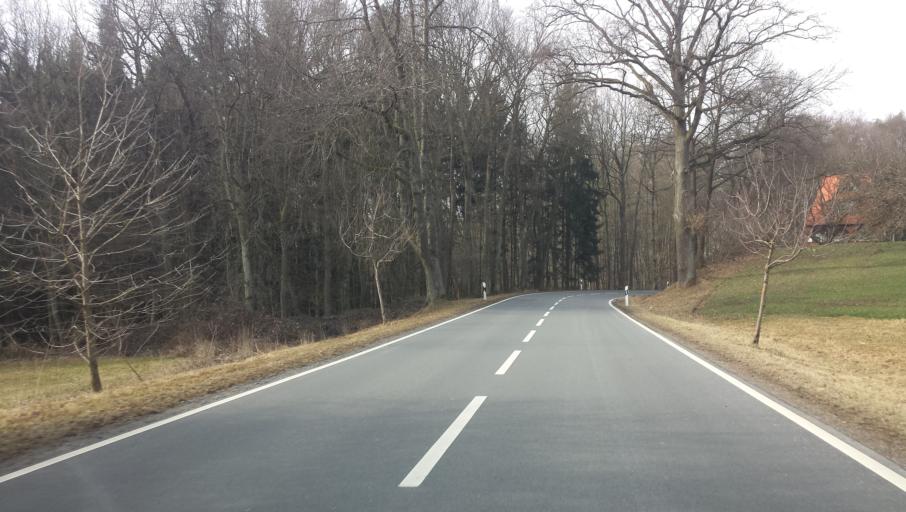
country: DE
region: Hesse
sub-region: Regierungsbezirk Darmstadt
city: Frankisch-Crumbach
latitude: 49.7141
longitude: 8.8933
